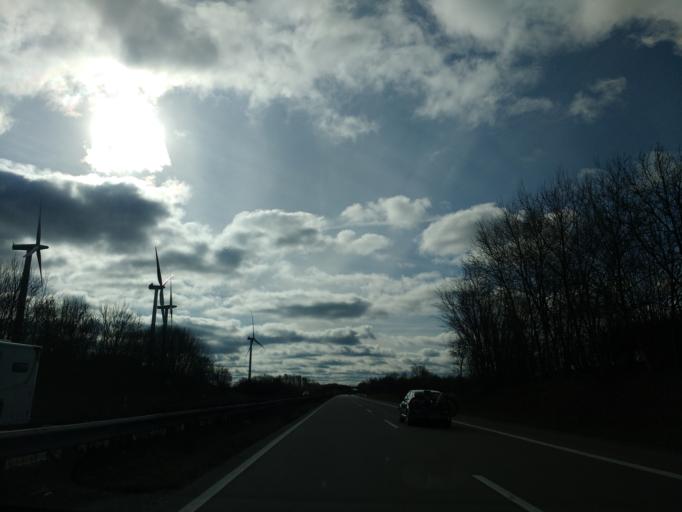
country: DE
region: Lower Saxony
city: Langen
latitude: 53.6383
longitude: 8.6642
